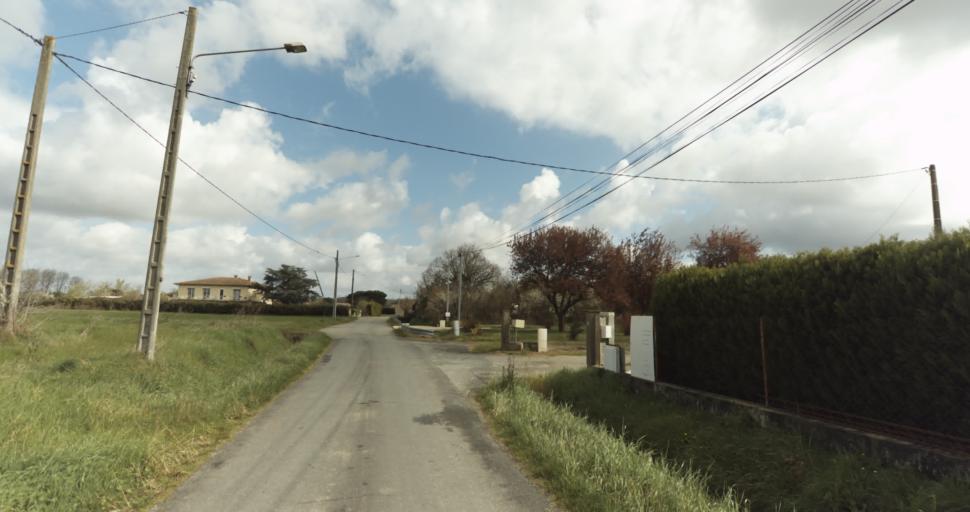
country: FR
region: Midi-Pyrenees
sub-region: Departement de la Haute-Garonne
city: Auterive
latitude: 43.3454
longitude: 1.4598
